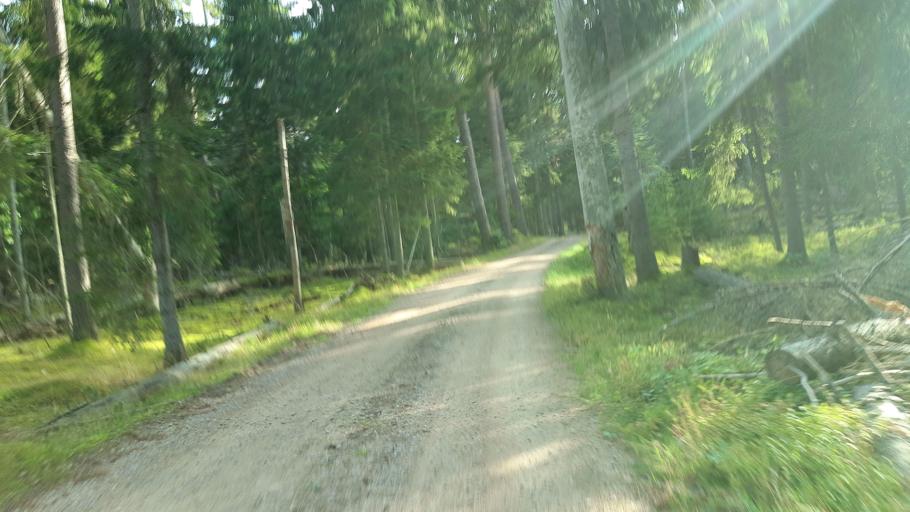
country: SE
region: Blekinge
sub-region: Ronneby Kommun
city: Kallinge
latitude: 56.2357
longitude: 15.3862
